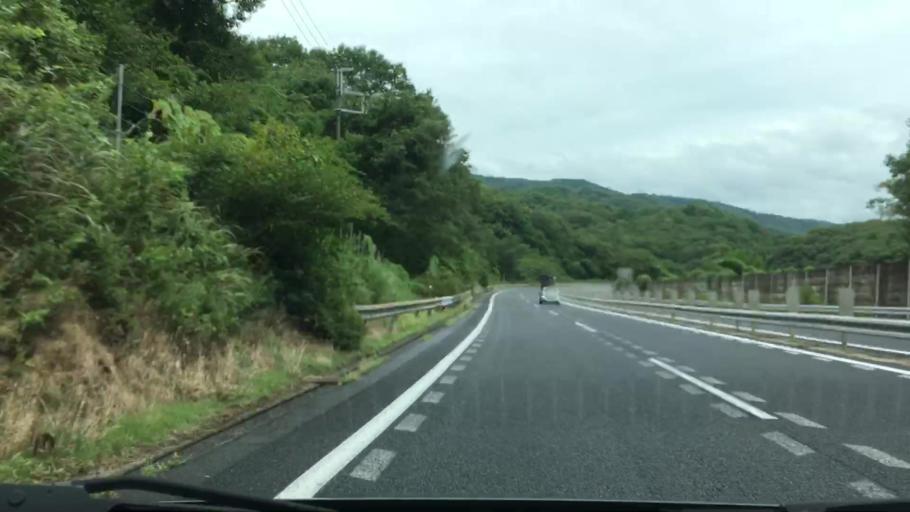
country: JP
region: Hyogo
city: Yamazakicho-nakabirose
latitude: 35.0077
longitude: 134.3263
